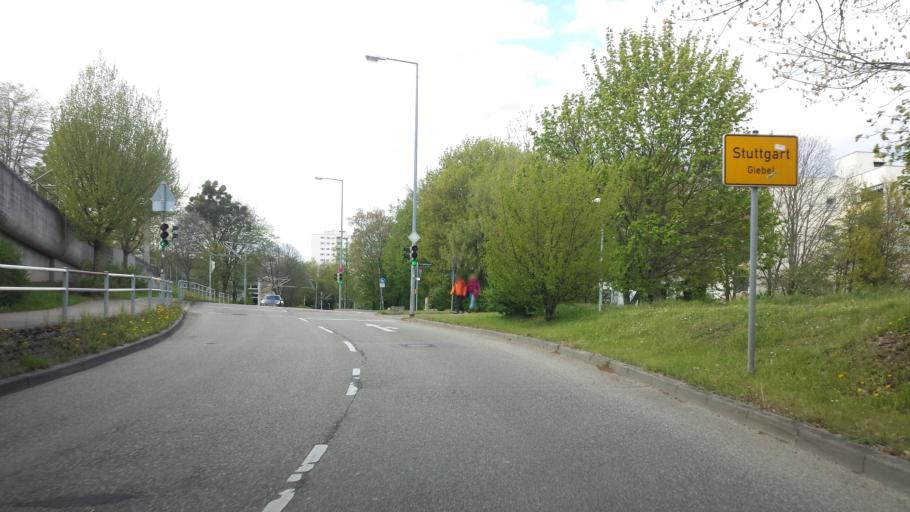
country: DE
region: Baden-Wuerttemberg
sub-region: Regierungsbezirk Stuttgart
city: Gerlingen
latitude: 48.8029
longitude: 9.0973
